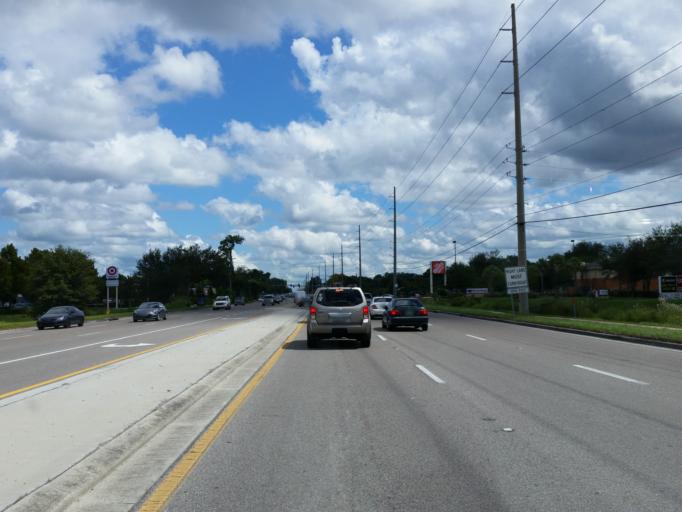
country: US
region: Florida
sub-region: Hillsborough County
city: Riverview
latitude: 27.8937
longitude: -82.3346
